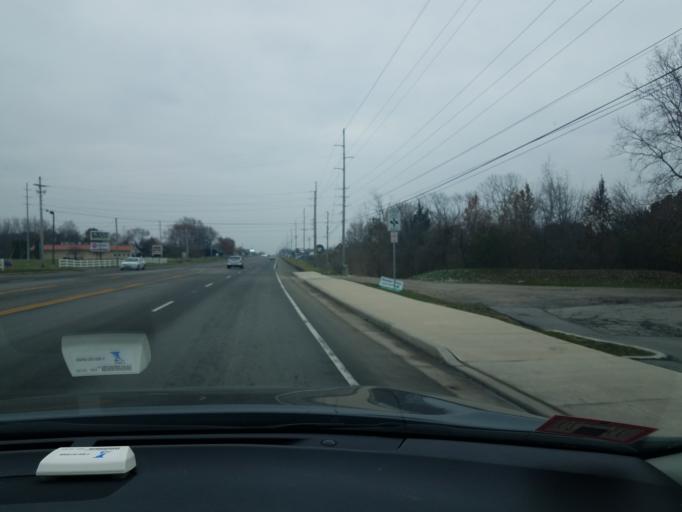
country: US
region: Ohio
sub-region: Erie County
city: Sandusky
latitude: 41.3948
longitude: -82.6512
